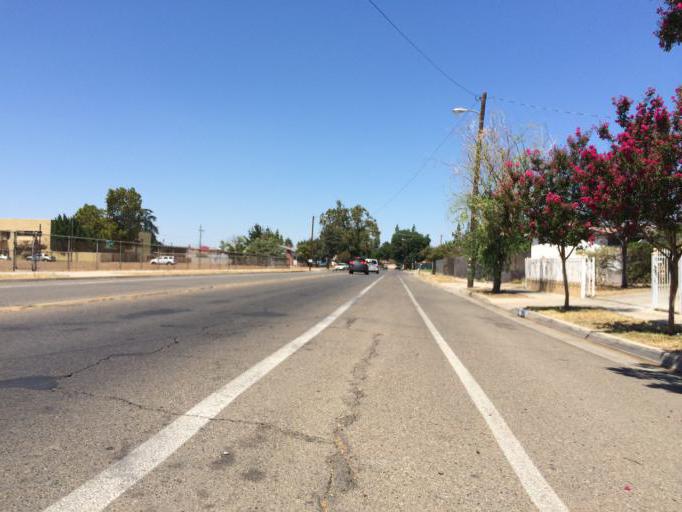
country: US
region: California
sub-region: Fresno County
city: Fresno
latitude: 36.7340
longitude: -119.7736
